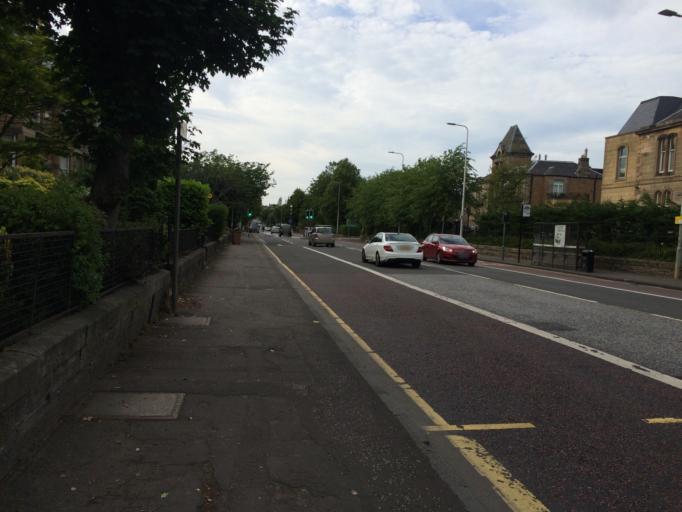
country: GB
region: Scotland
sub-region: Edinburgh
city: Edinburgh
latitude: 55.9287
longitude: -3.1693
